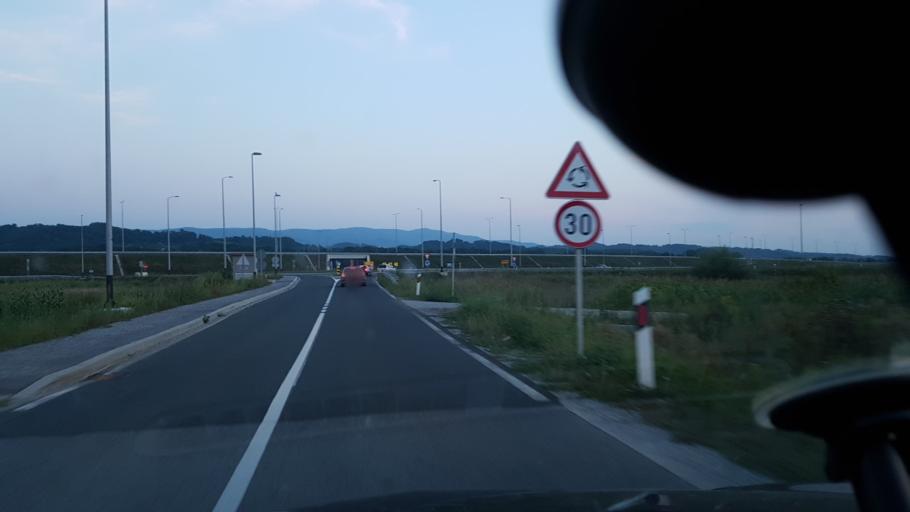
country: HR
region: Krapinsko-Zagorska
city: Bedekovcina
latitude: 46.0348
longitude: 15.9945
